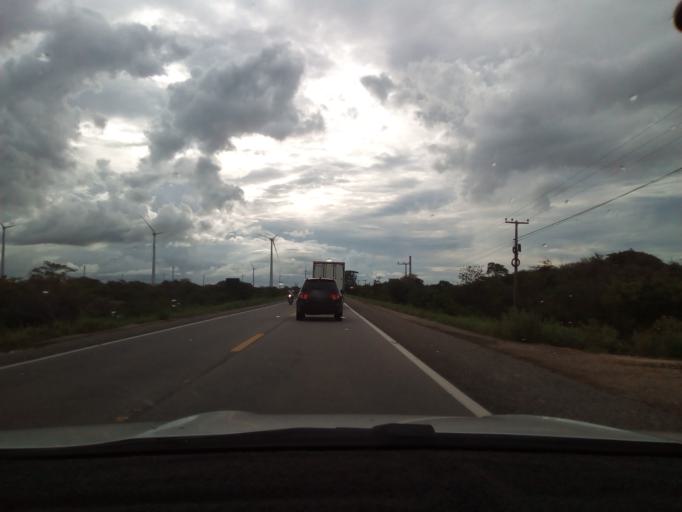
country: BR
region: Ceara
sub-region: Aracati
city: Aracati
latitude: -4.5970
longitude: -37.6767
